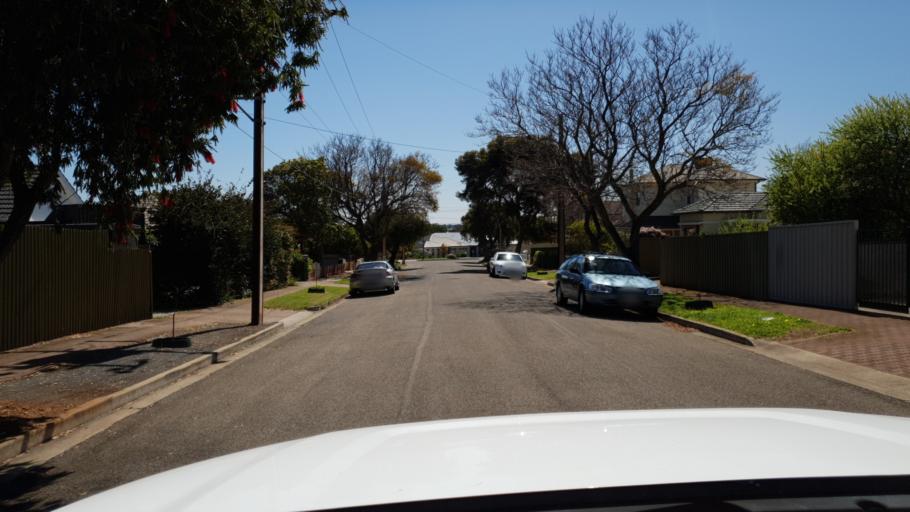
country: AU
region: South Australia
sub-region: Holdfast Bay
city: Seacliff Park
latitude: -35.0298
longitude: 138.5300
